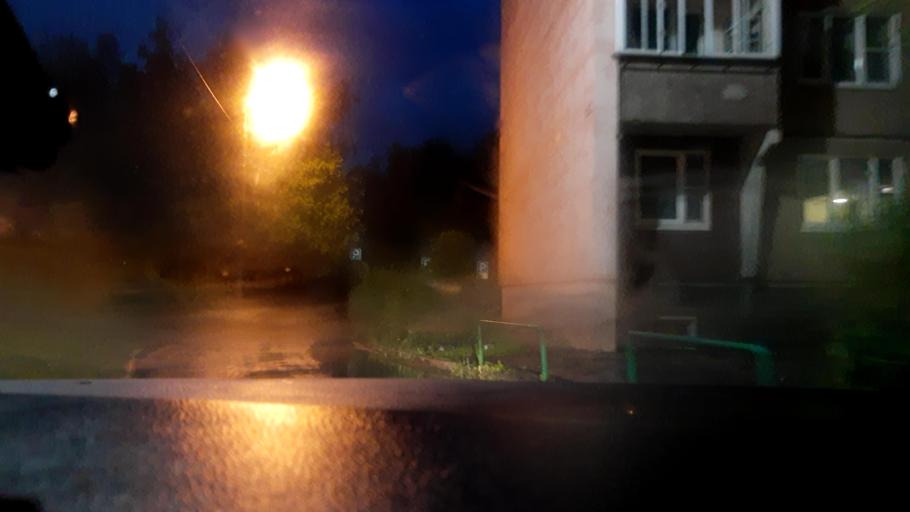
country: RU
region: Moskovskaya
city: Nakhabino
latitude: 55.8513
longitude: 37.1702
